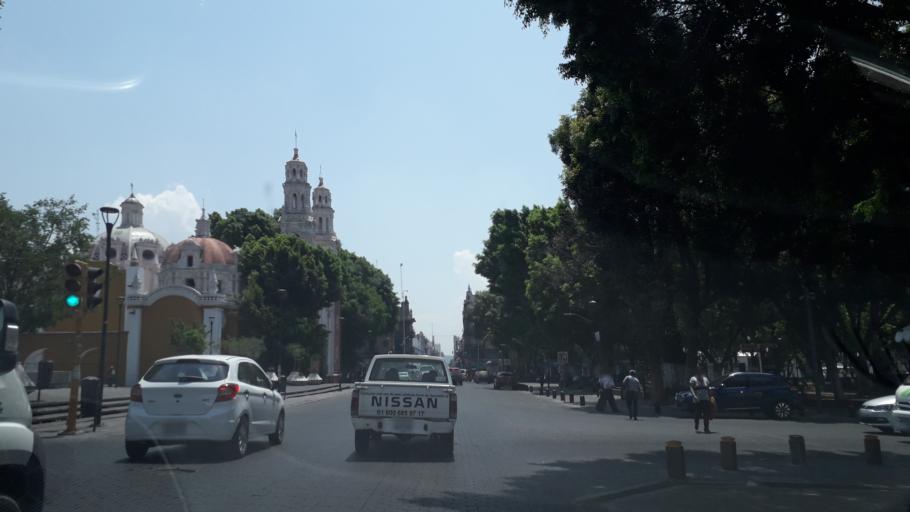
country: MX
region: Puebla
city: Puebla
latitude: 19.0489
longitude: -98.2075
